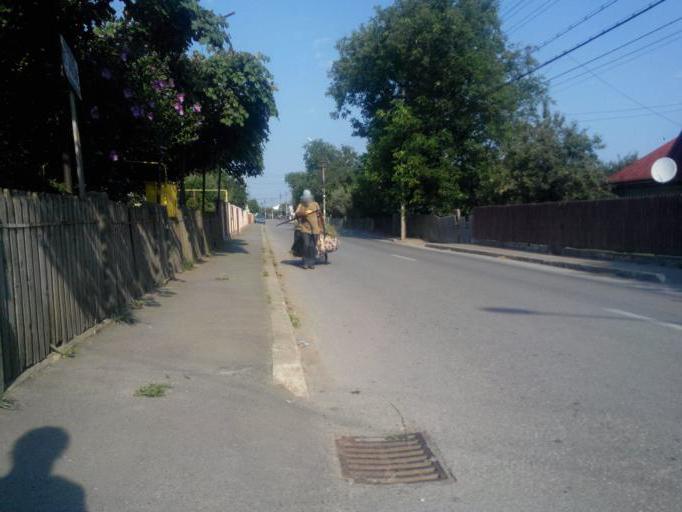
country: RO
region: Suceava
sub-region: Municipiul Falticeni
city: Falticeni
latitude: 47.4674
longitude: 26.2806
